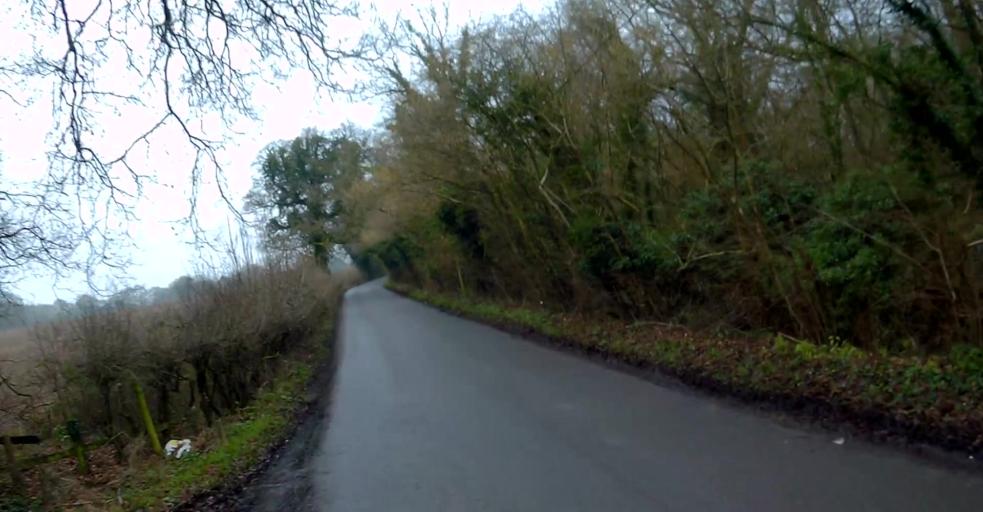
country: GB
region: England
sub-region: Hampshire
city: Hook
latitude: 51.2842
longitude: -0.9975
